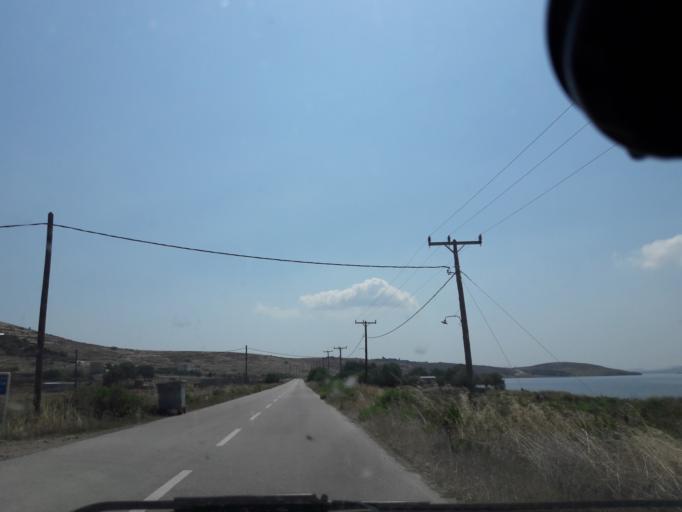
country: GR
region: North Aegean
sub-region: Nomos Lesvou
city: Myrina
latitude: 39.8631
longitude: 25.2640
